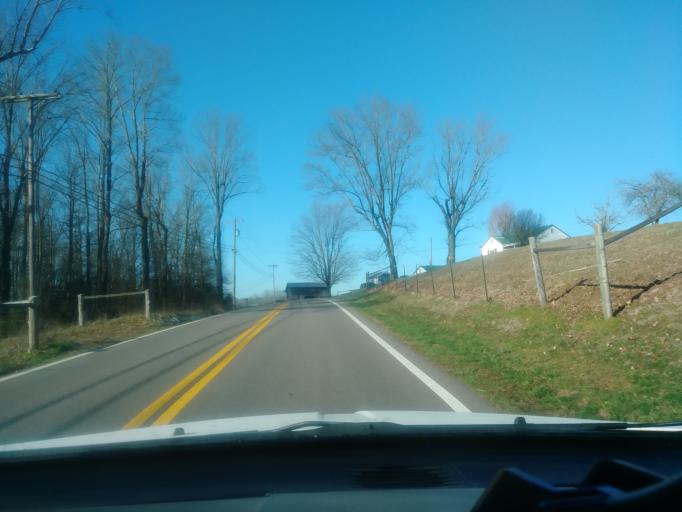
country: US
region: Tennessee
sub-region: Greene County
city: Mosheim
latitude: 36.1172
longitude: -82.9445
